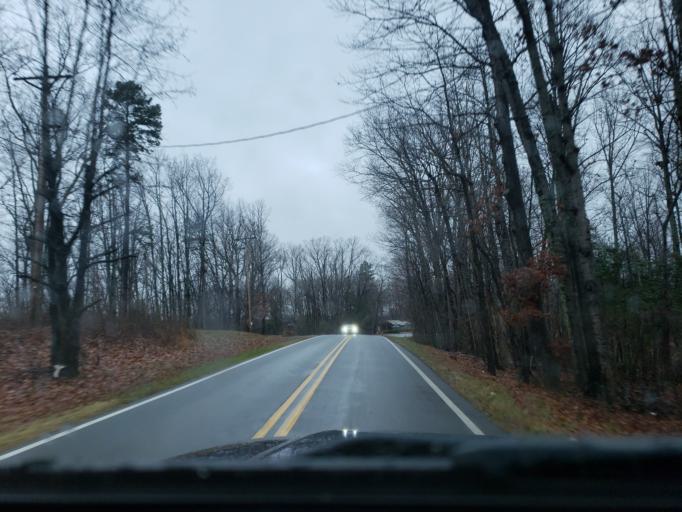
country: US
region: North Carolina
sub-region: Cleveland County
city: White Plains
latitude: 35.1919
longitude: -81.3780
